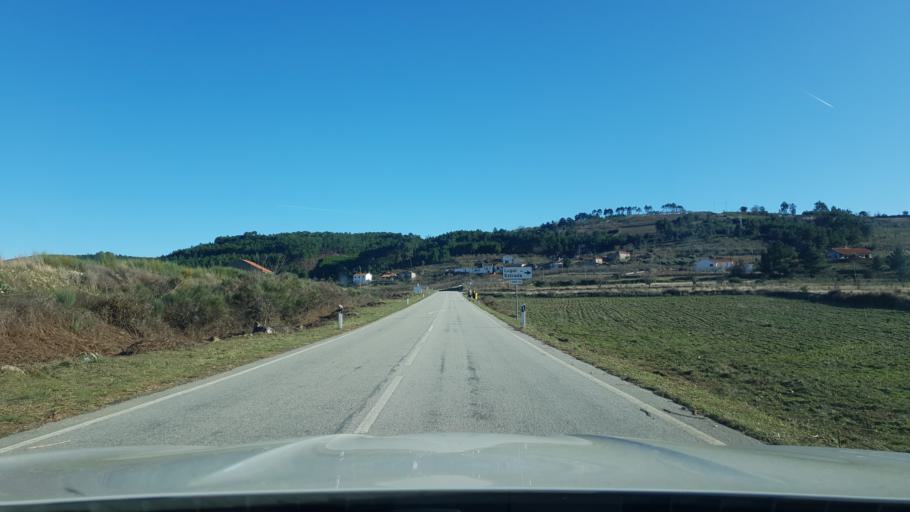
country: PT
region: Braganca
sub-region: Freixo de Espada A Cinta
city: Freixo de Espada a Cinta
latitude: 41.1827
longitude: -6.8232
